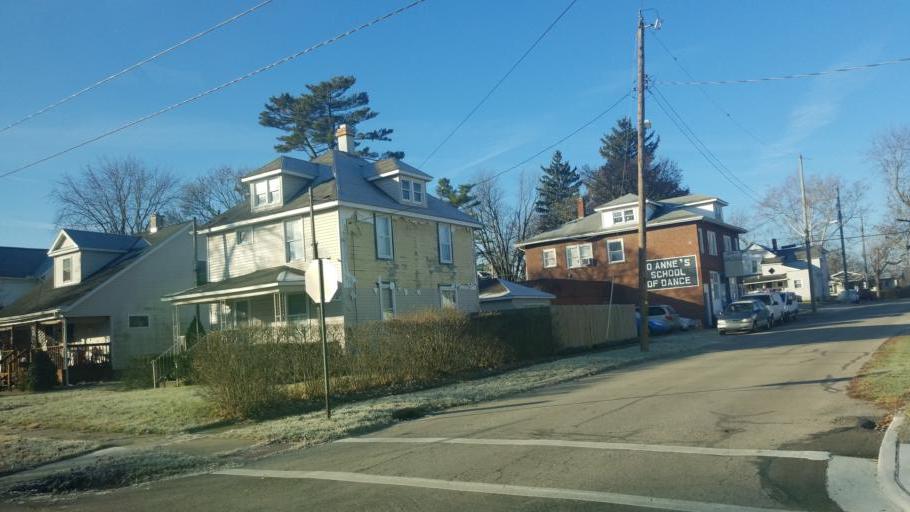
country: US
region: Ohio
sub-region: Marion County
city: Marion
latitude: 40.5858
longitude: -83.1135
